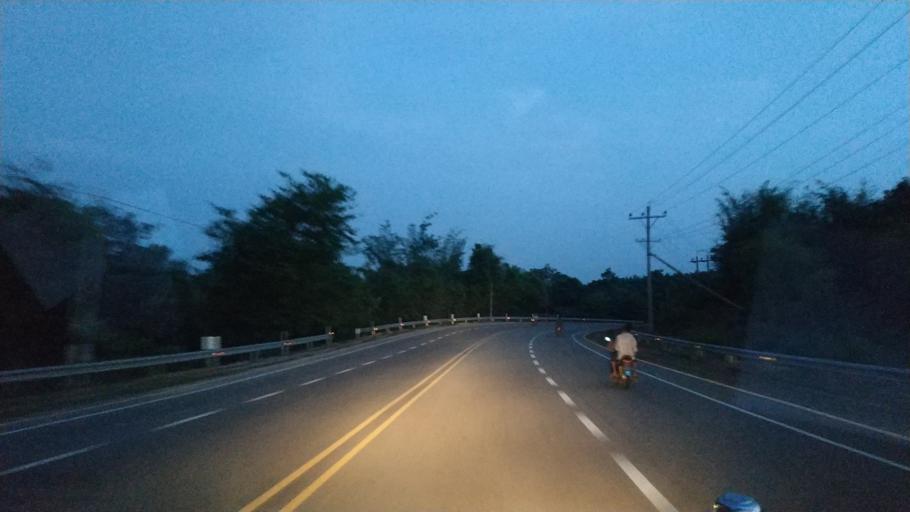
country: MM
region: Mon
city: Kyaikto
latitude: 17.3541
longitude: 97.0399
